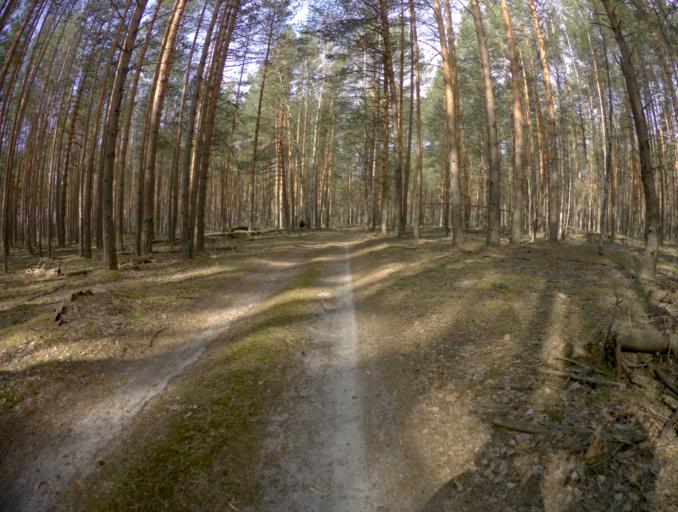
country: RU
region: Vladimir
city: Mezinovskiy
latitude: 55.6032
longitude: 40.3965
